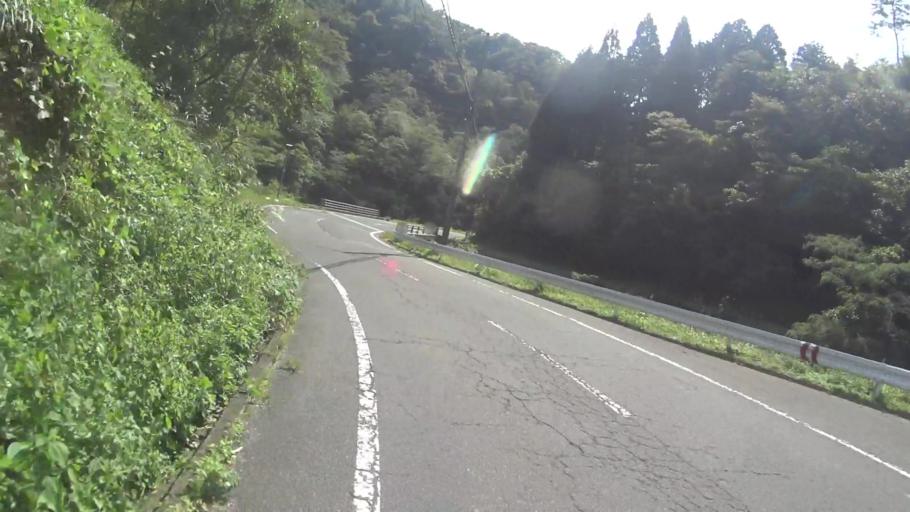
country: JP
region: Kyoto
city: Miyazu
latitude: 35.6947
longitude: 135.1700
